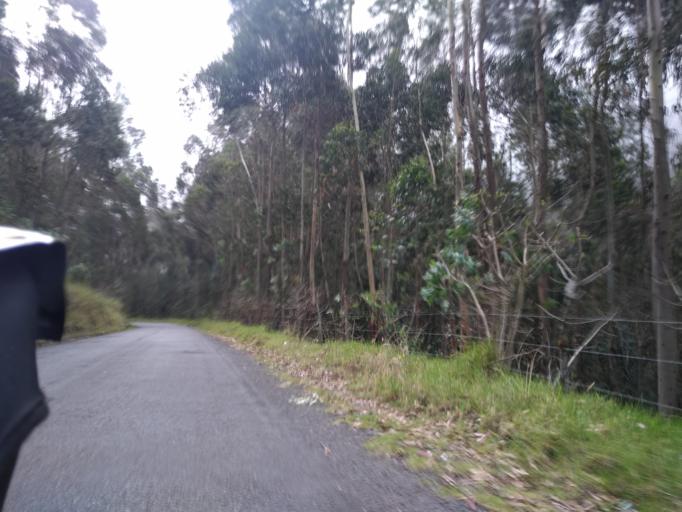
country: EC
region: Cotopaxi
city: Saquisili
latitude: -0.6925
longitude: -78.8210
